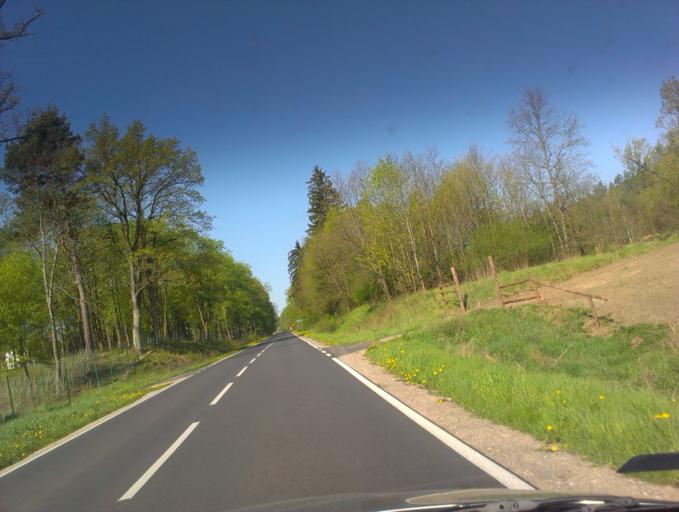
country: PL
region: West Pomeranian Voivodeship
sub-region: Powiat swidwinski
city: Polczyn-Zdroj
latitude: 53.7704
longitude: 16.1432
